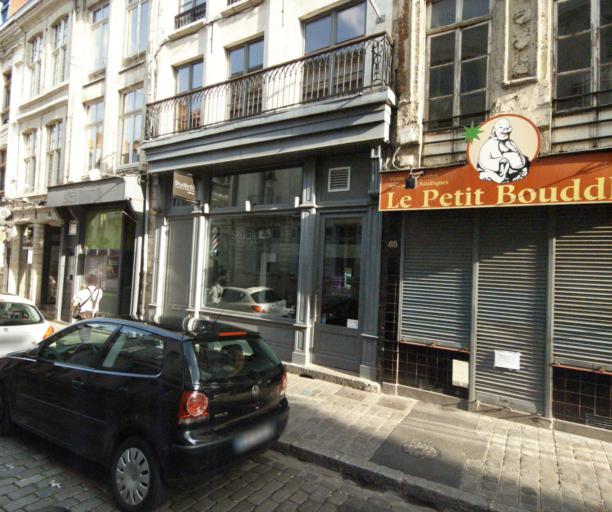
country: FR
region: Nord-Pas-de-Calais
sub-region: Departement du Nord
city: Lille
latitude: 50.6387
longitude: 3.0604
